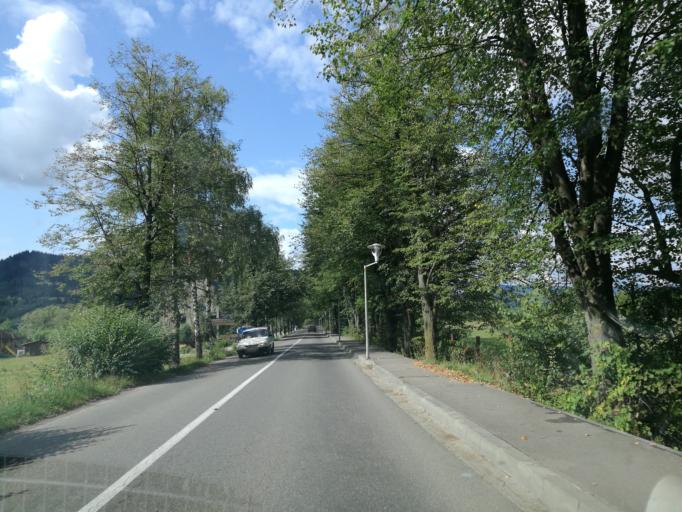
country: RO
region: Suceava
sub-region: Oras Gura Humorului
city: Gura Humorului
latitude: 47.5424
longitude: 25.8687
